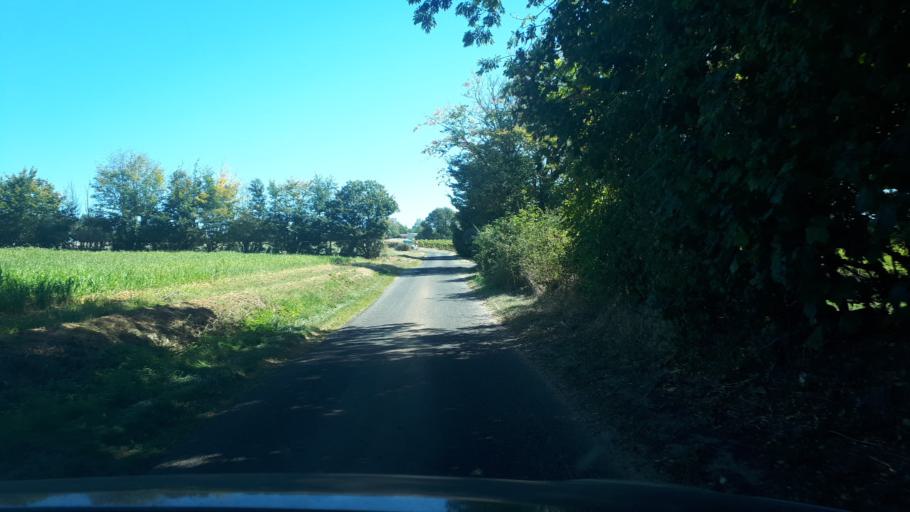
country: FR
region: Centre
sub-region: Departement du Cher
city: Sancerre
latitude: 47.3096
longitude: 2.7447
